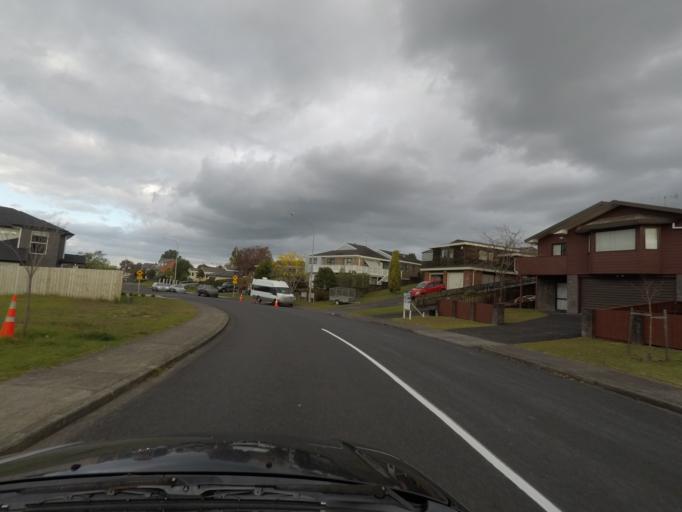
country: NZ
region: Auckland
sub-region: Auckland
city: Rosebank
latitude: -36.8284
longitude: 174.6249
